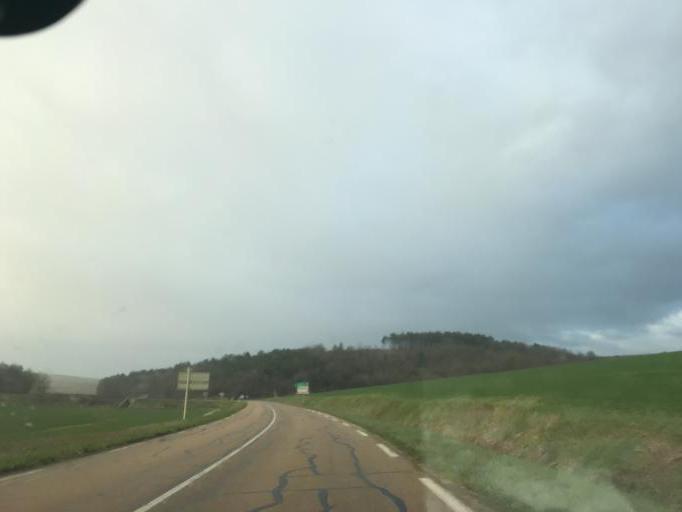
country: FR
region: Bourgogne
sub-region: Departement de l'Yonne
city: Fontenailles
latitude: 47.6260
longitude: 3.4930
